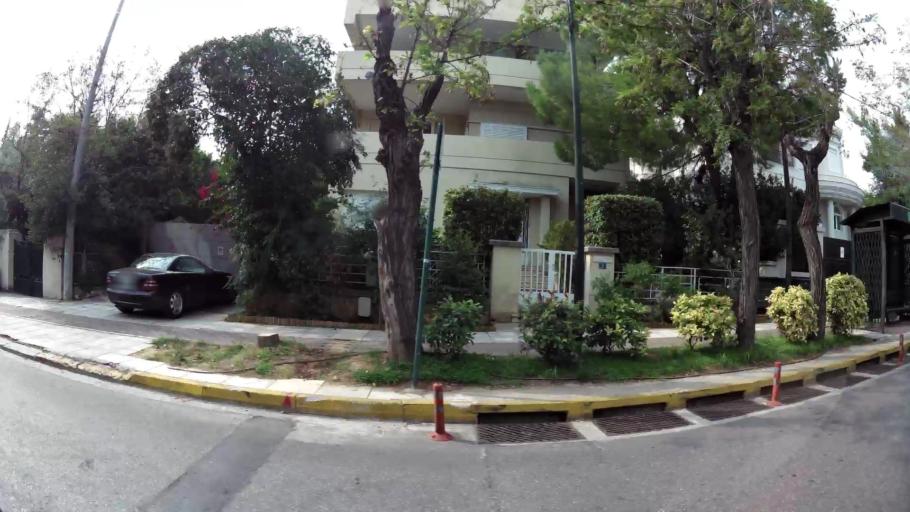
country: GR
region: Attica
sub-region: Nomarchia Athinas
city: Psychiko
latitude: 38.0058
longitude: 23.7751
